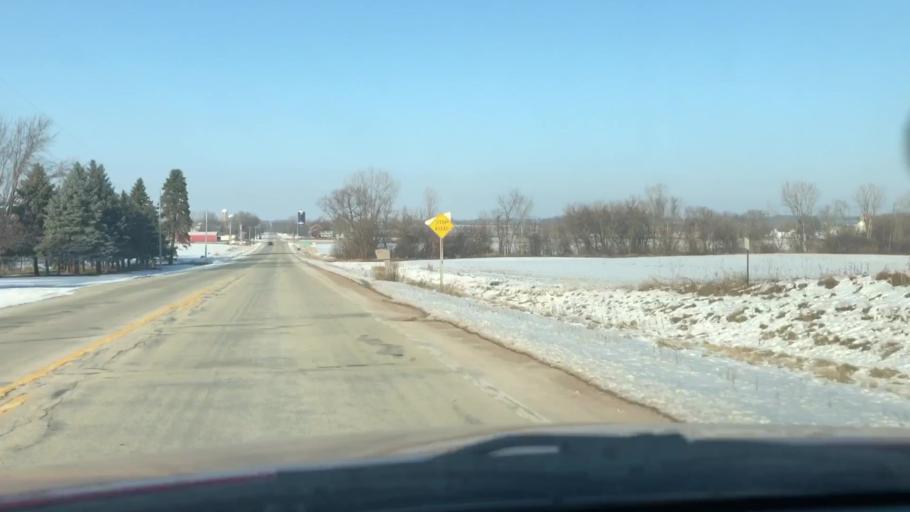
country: US
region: Wisconsin
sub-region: Outagamie County
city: Kimberly
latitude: 44.3833
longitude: -88.3747
